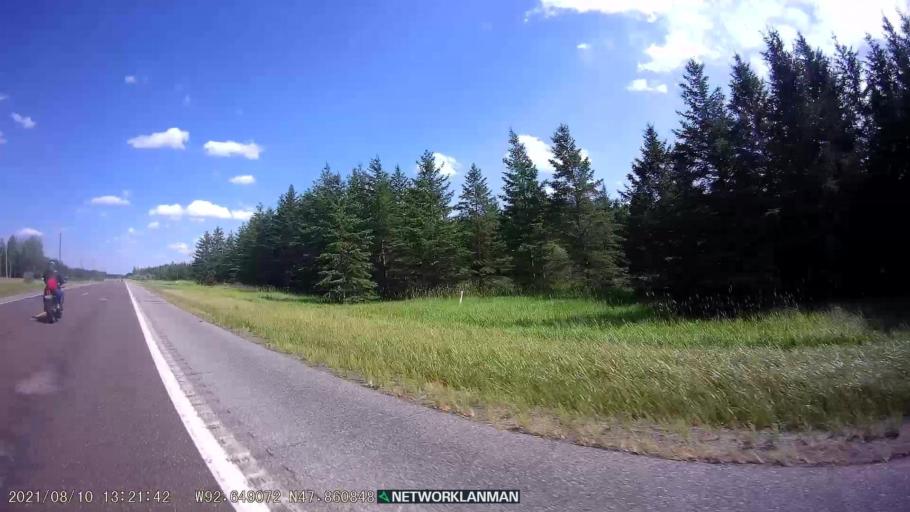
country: US
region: Minnesota
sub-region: Saint Louis County
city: Mountain Iron
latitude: 47.8612
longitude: -92.6488
